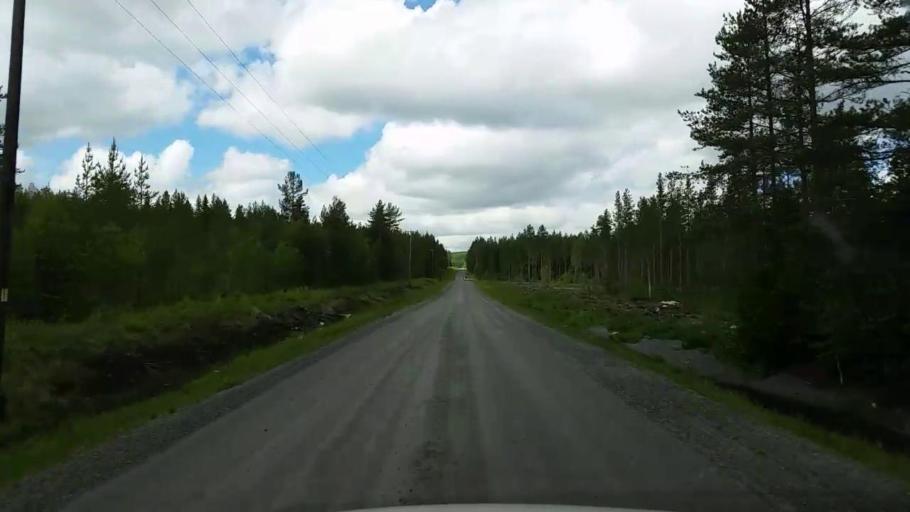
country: SE
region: Gaevleborg
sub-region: Bollnas Kommun
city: Vittsjo
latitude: 61.0810
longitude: 16.2594
